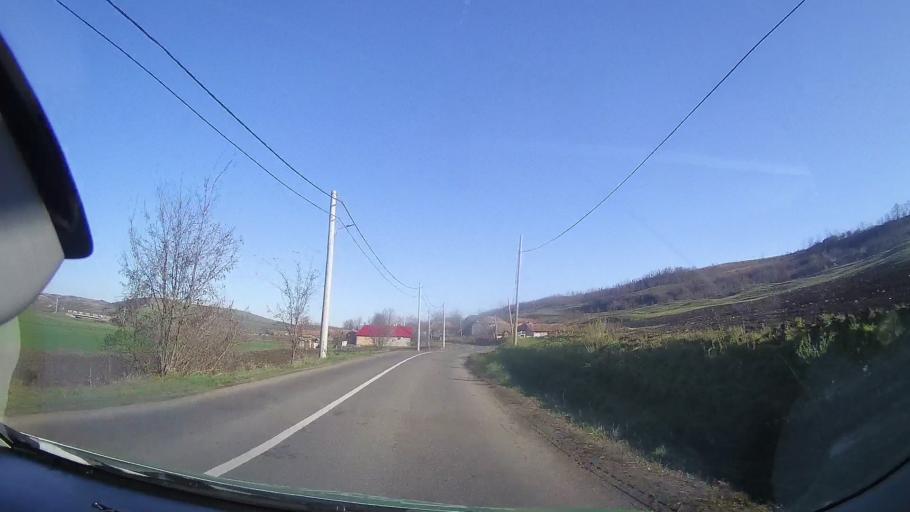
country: RO
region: Mures
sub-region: Comuna Band
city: Band
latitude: 46.5774
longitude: 24.3508
